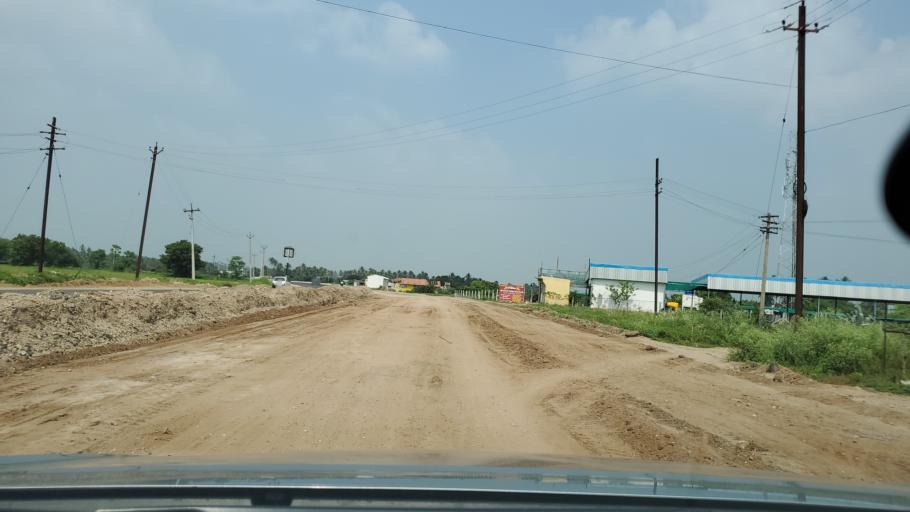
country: IN
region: Tamil Nadu
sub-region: Tiruppur
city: Kangayam
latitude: 10.9190
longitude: 77.4511
